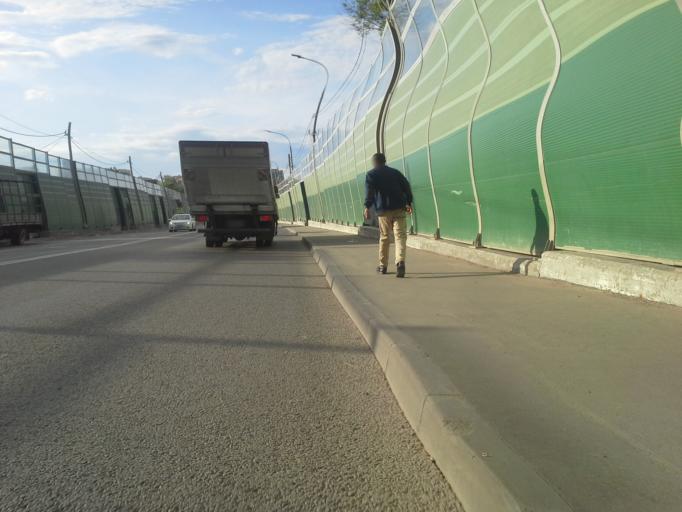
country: RU
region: Moscow
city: Novo-Peredelkino
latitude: 55.6274
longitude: 37.3373
